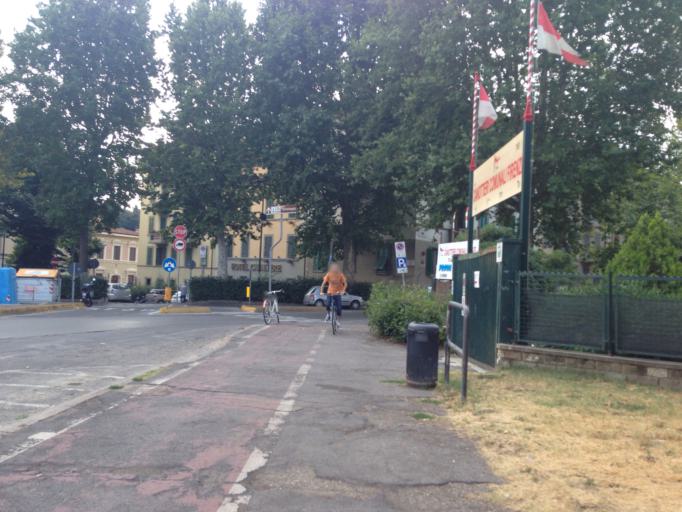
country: IT
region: Tuscany
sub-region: Province of Florence
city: Grassina Ponte a Ema
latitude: 43.7640
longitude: 11.2814
